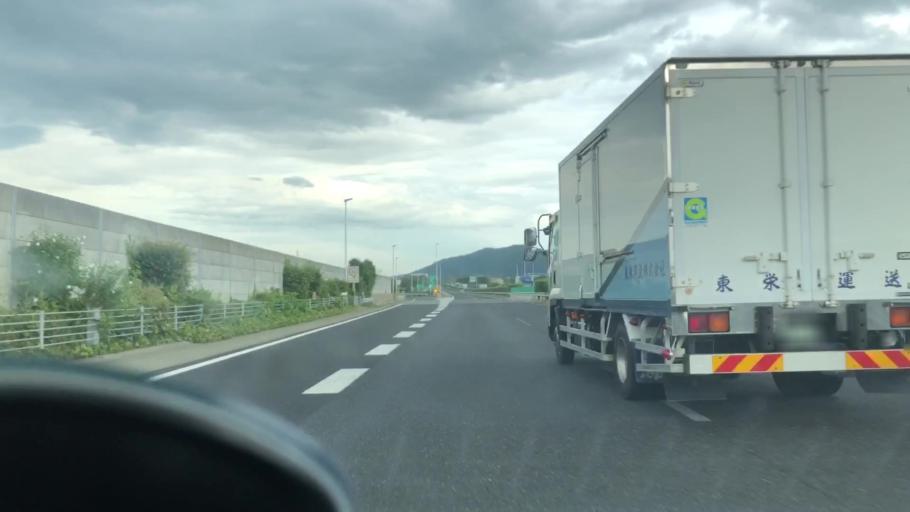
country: JP
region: Hyogo
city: Himeji
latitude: 34.9491
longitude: 134.7610
